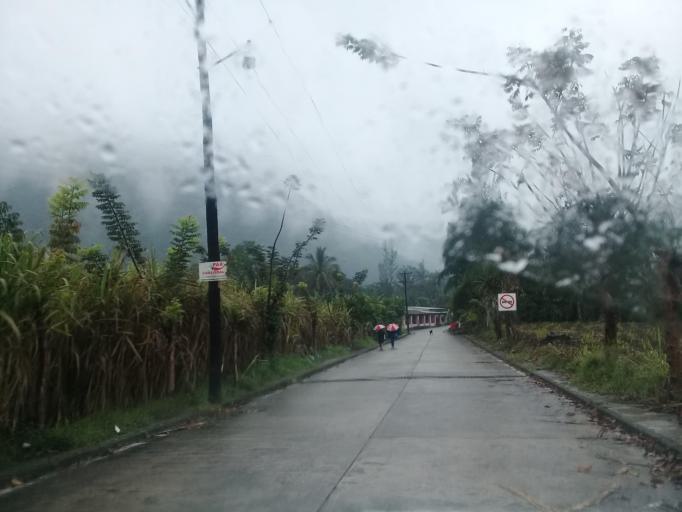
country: MX
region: Veracruz
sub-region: Amatlan de los Reyes
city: Centro de Readaptacion Social
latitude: 18.8019
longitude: -96.9495
